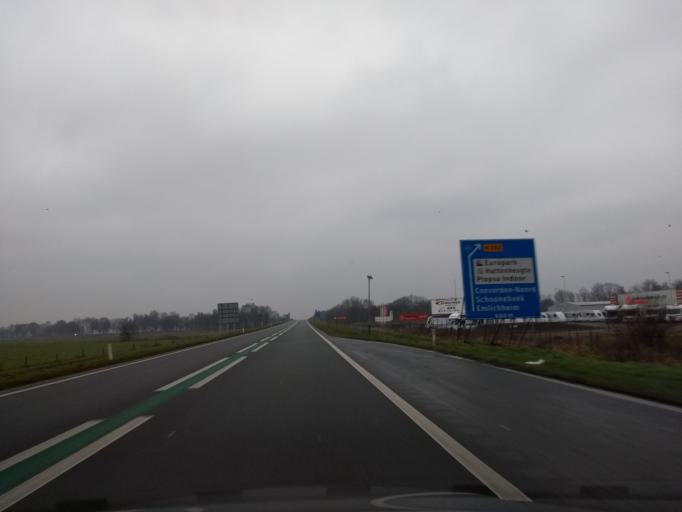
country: NL
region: Drenthe
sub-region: Gemeente Coevorden
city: Coevorden
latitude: 52.6664
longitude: 6.7218
